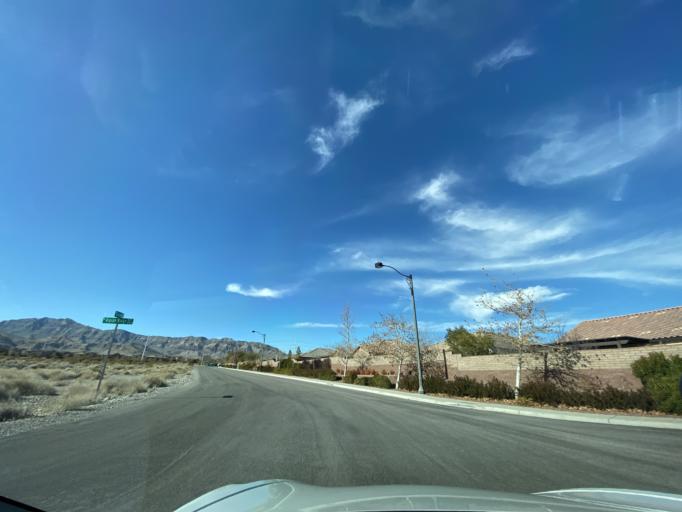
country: US
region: Nevada
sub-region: Clark County
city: Summerlin South
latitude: 36.2864
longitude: -115.3242
